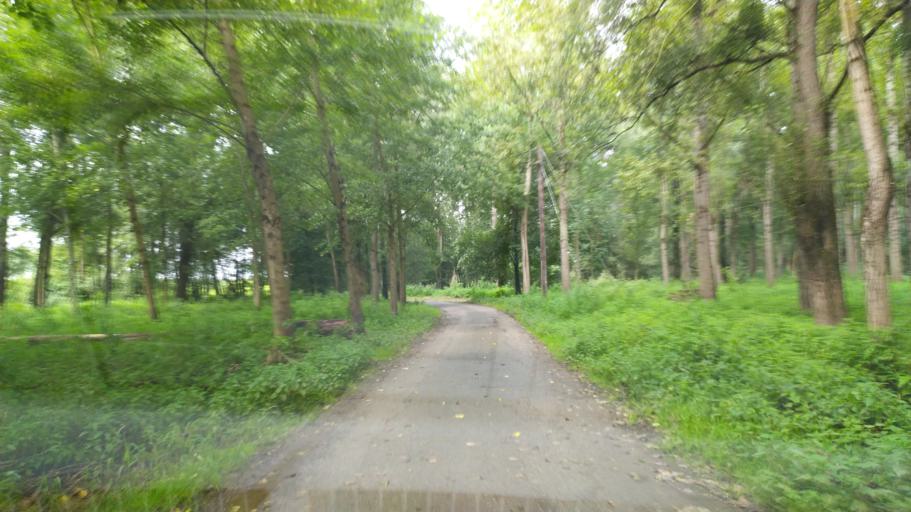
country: AT
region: Upper Austria
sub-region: Politischer Bezirk Perg
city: Bad Kreuzen
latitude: 48.1998
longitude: 14.7896
